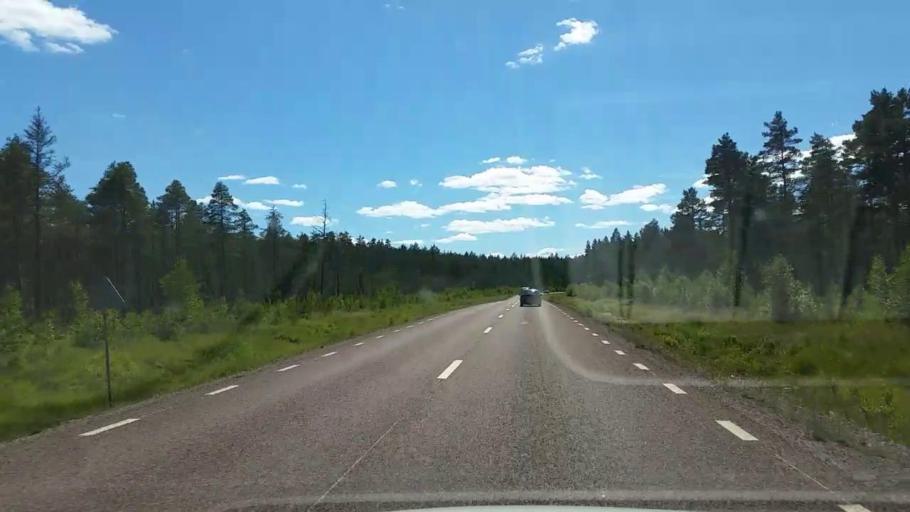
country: SE
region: Gaevleborg
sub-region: Ovanakers Kommun
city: Edsbyn
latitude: 61.2838
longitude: 15.9047
